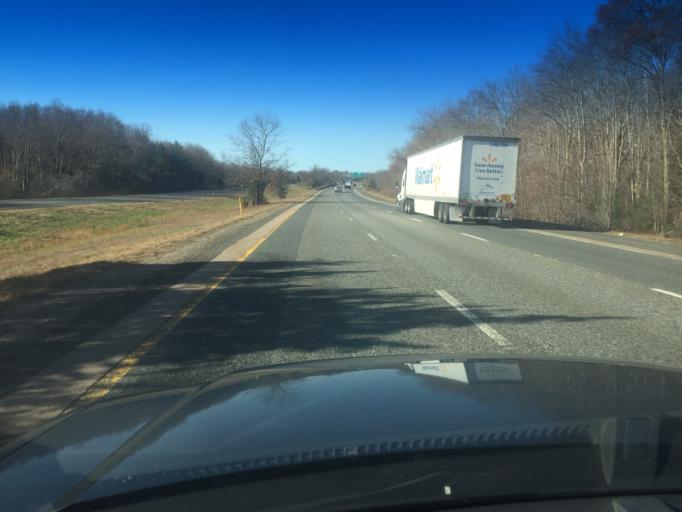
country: US
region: Massachusetts
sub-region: Bristol County
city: Attleboro
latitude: 41.9504
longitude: -71.3358
